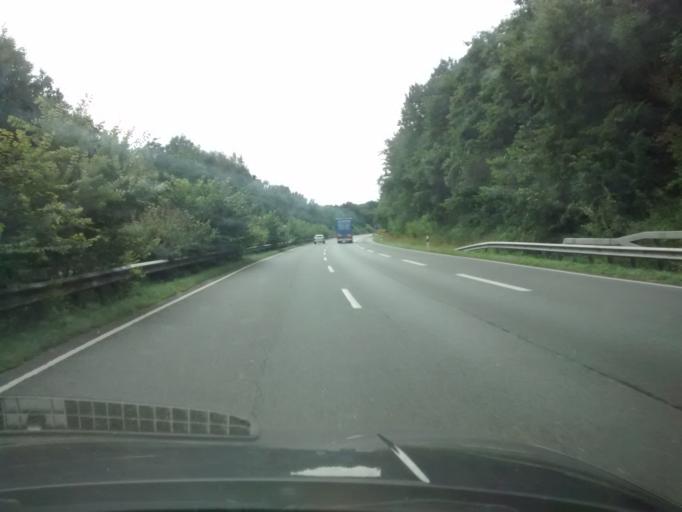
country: DE
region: Lower Saxony
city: Cloppenburg
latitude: 52.8353
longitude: 8.0210
